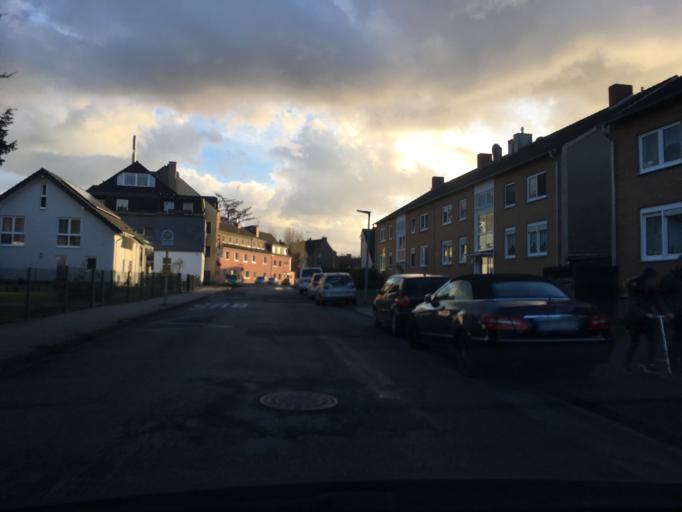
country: DE
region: North Rhine-Westphalia
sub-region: Regierungsbezirk Dusseldorf
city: Oberhausen
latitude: 51.4731
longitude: 6.8965
